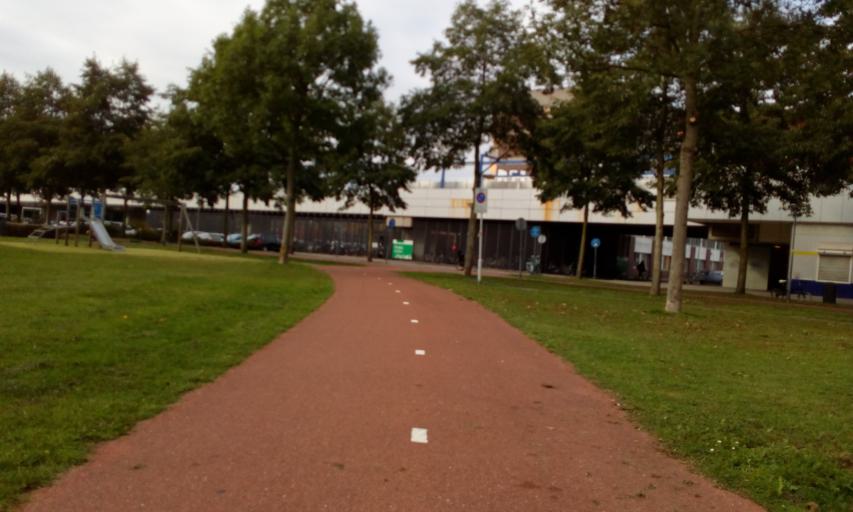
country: NL
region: South Holland
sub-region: Gemeente Spijkenisse
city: Spijkenisse
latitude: 51.8603
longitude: 4.3675
